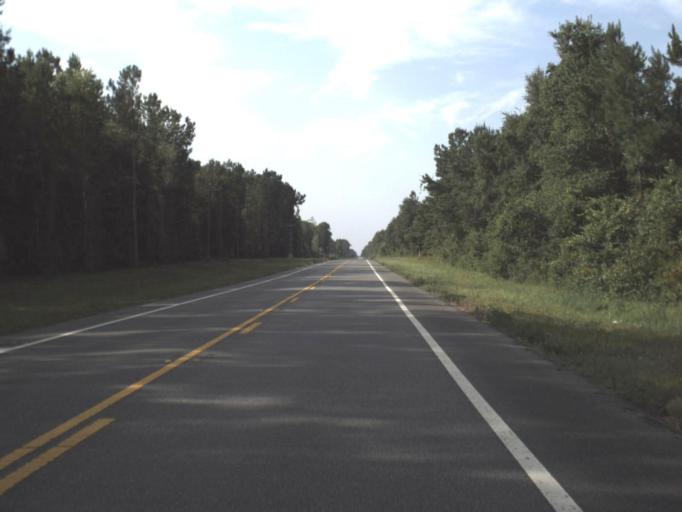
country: US
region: Florida
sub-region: Taylor County
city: Perry
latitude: 30.2670
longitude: -83.6269
